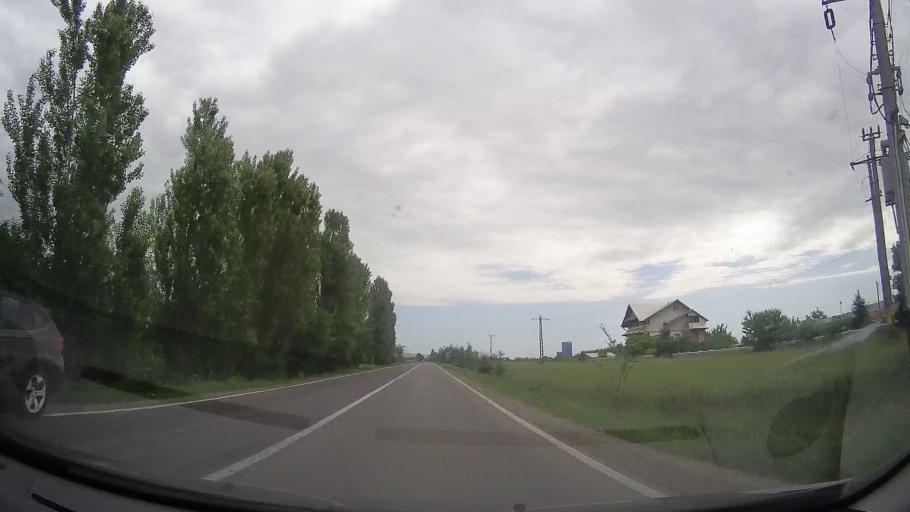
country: RO
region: Prahova
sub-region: Comuna Berceni
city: Corlatesti
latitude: 44.9023
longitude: 26.0673
